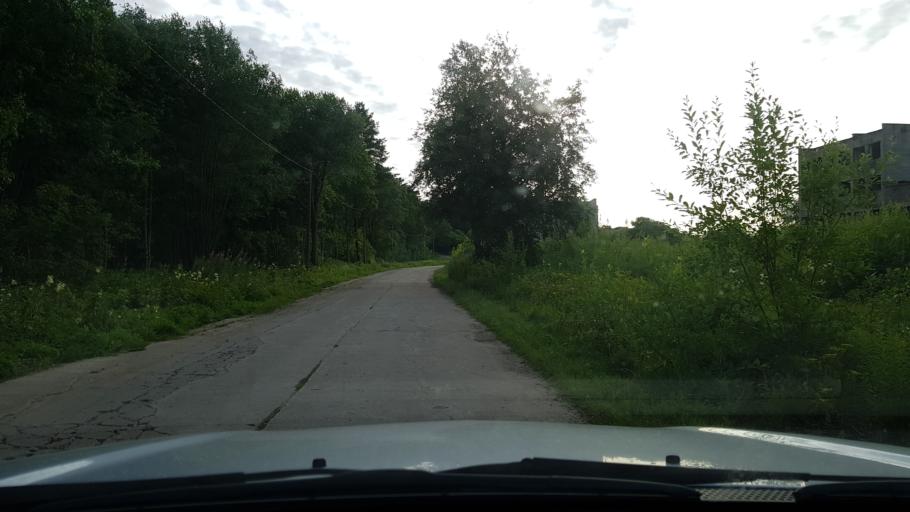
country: EE
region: Ida-Virumaa
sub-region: Narva-Joesuu linn
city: Narva-Joesuu
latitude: 59.4588
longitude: 28.0592
